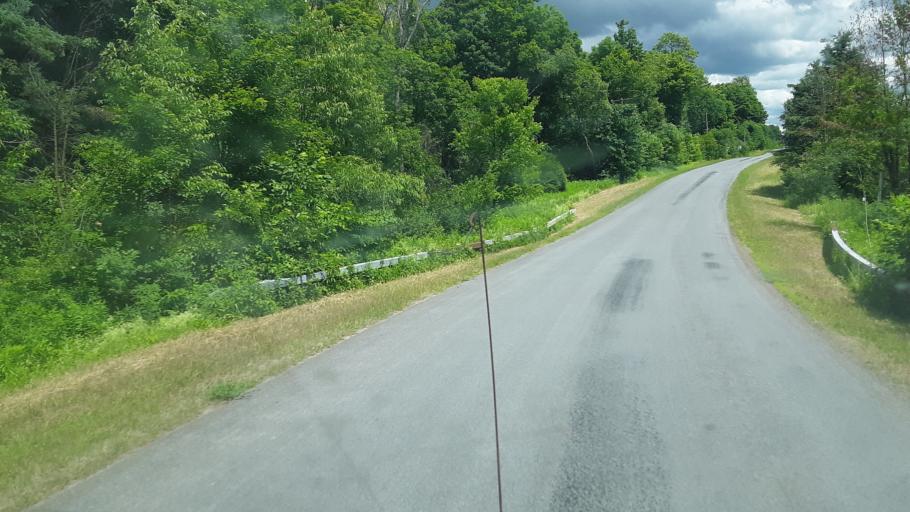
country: US
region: New York
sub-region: Oneida County
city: Rome
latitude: 43.3939
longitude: -75.5043
